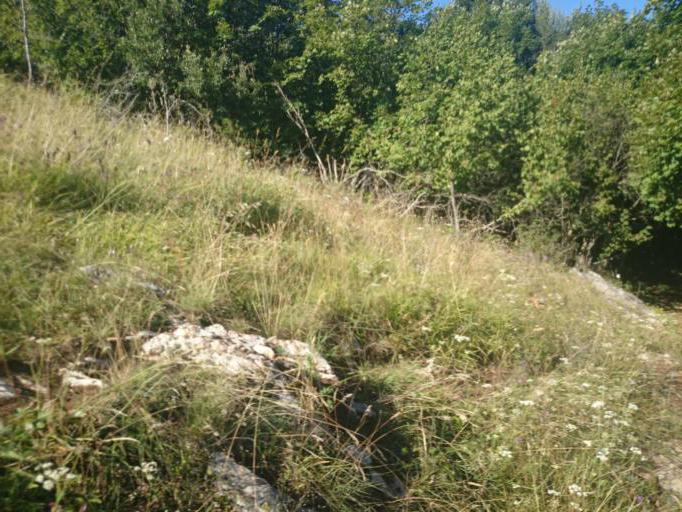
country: AL
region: Diber
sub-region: Rrethi i Bulqizes
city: Martanesh
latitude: 41.4009
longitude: 20.1716
